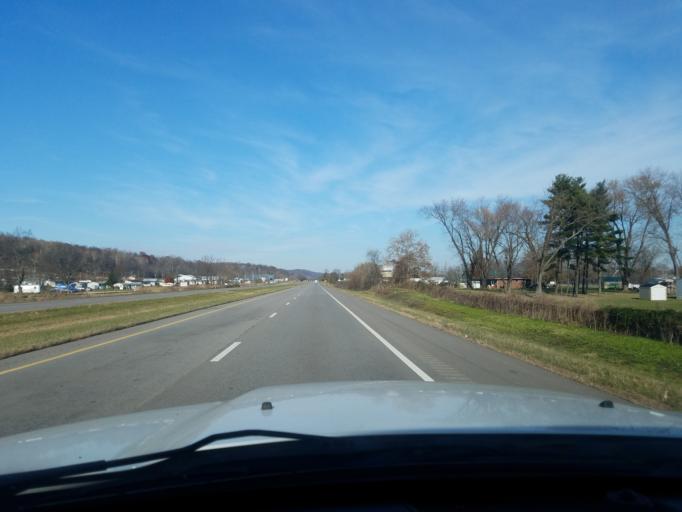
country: US
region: West Virginia
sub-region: Wood County
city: Vienna
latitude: 39.3131
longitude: -81.5650
